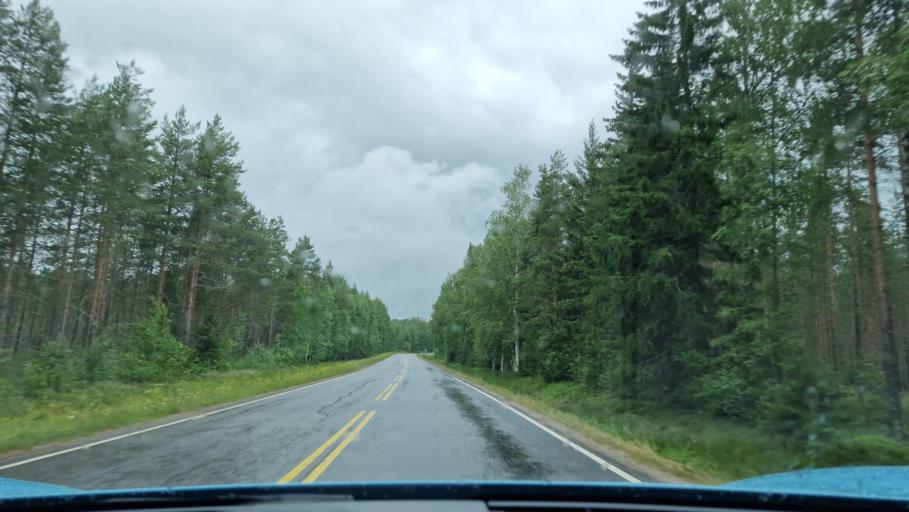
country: FI
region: Southern Ostrobothnia
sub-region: Jaerviseutu
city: Soini
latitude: 62.7901
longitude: 24.3814
